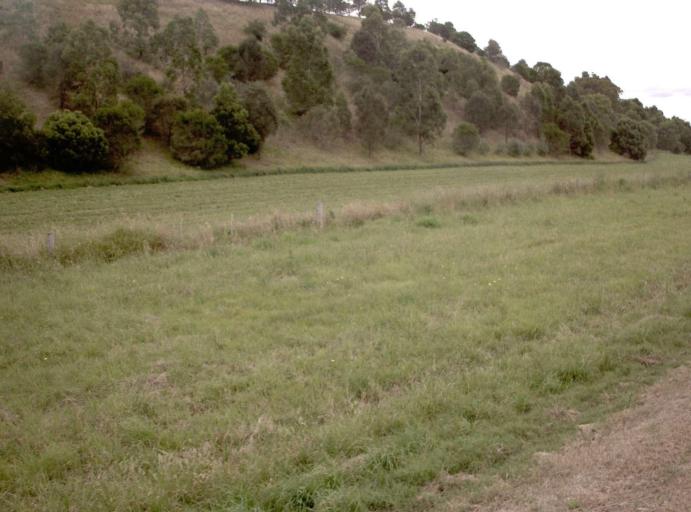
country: AU
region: Victoria
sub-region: East Gippsland
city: Bairnsdale
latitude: -37.7933
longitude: 147.4067
